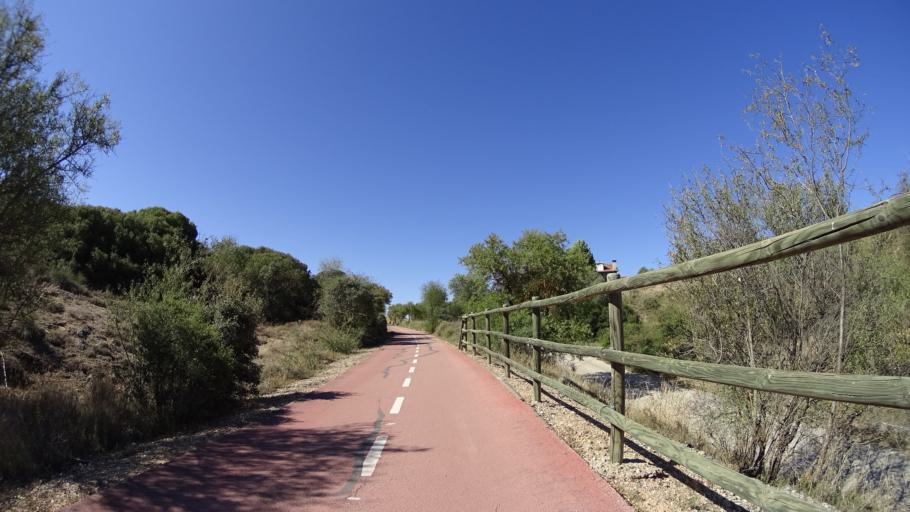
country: ES
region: Madrid
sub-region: Provincia de Madrid
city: Arganda
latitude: 40.2650
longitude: -3.4678
